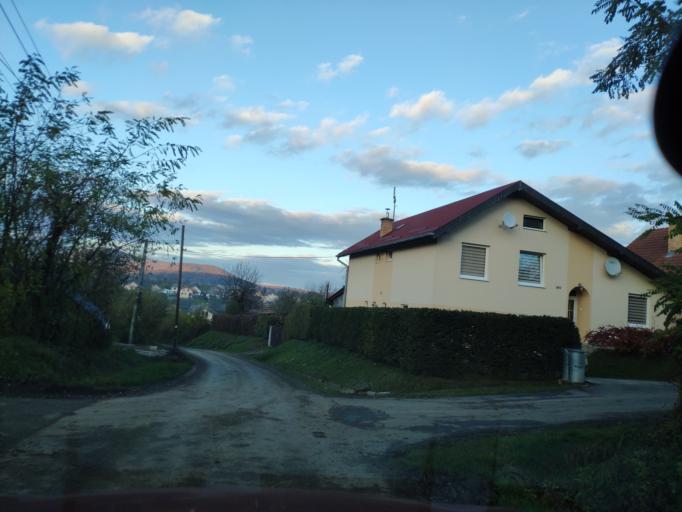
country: SK
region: Kosicky
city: Secovce
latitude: 48.6113
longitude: 21.5226
